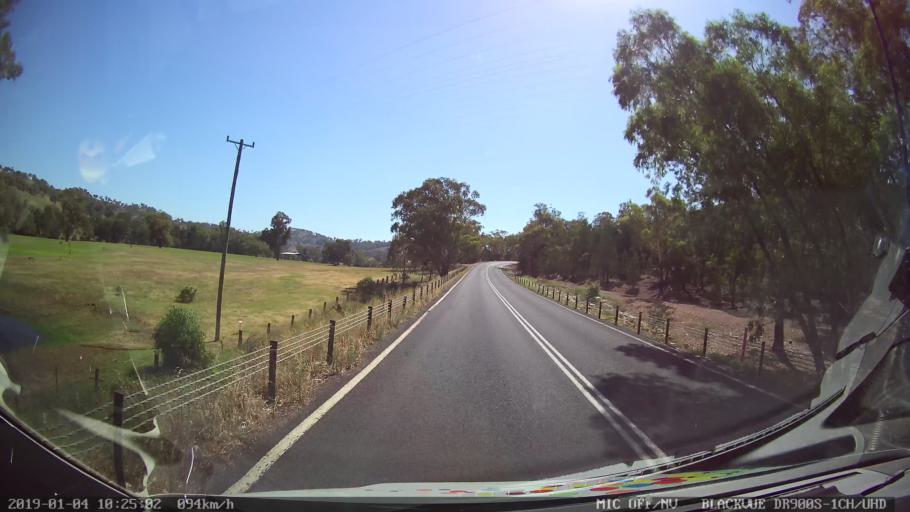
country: AU
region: New South Wales
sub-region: Cabonne
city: Canowindra
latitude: -33.3686
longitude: 148.5643
